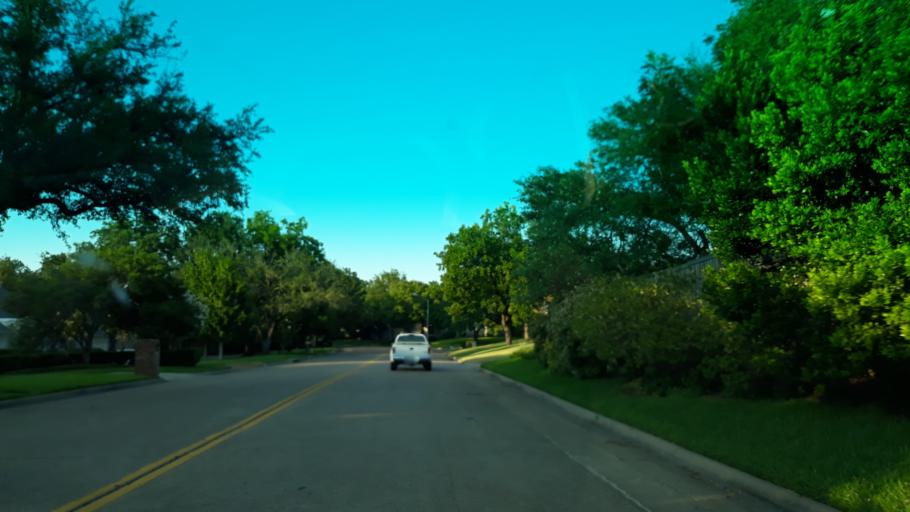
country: US
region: Texas
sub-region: Dallas County
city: Addison
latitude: 32.9478
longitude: -96.7934
